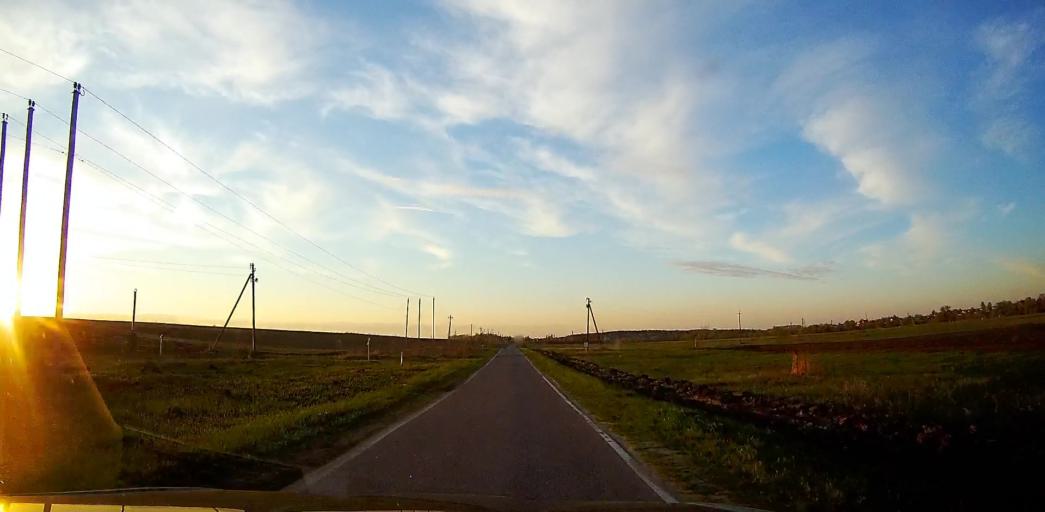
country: RU
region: Moskovskaya
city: Peski
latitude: 55.2189
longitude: 38.7383
